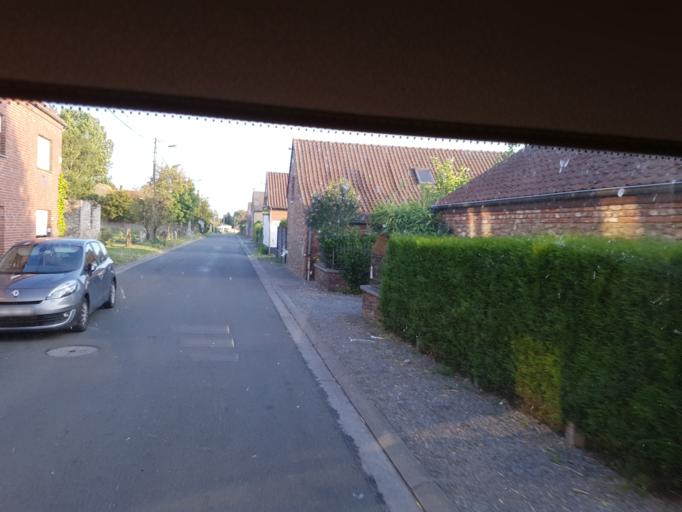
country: FR
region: Nord-Pas-de-Calais
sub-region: Departement du Nord
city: Hergnies
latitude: 50.5029
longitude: 3.5485
